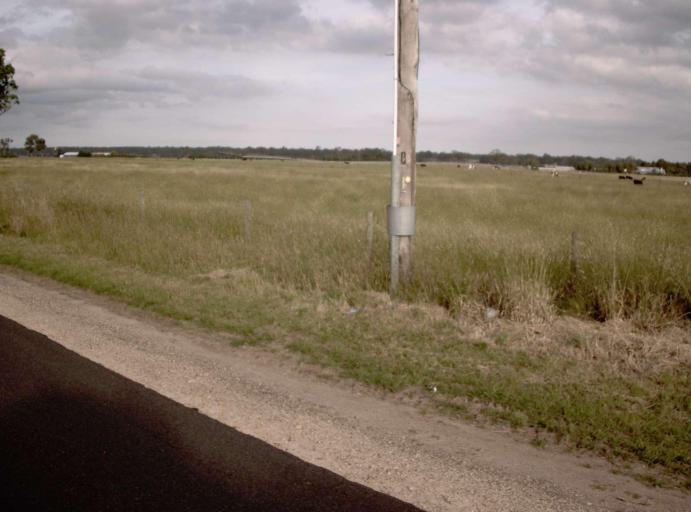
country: AU
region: Victoria
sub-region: Wellington
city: Sale
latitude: -37.8625
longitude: 147.0334
